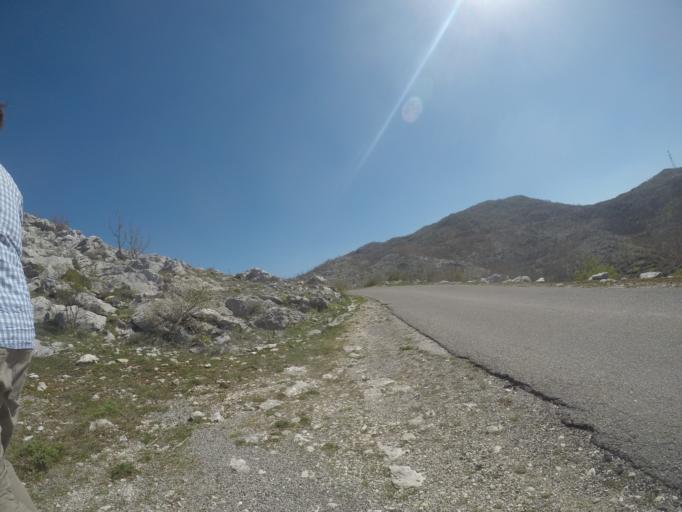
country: ME
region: Cetinje
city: Cetinje
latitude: 42.4963
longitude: 18.8763
